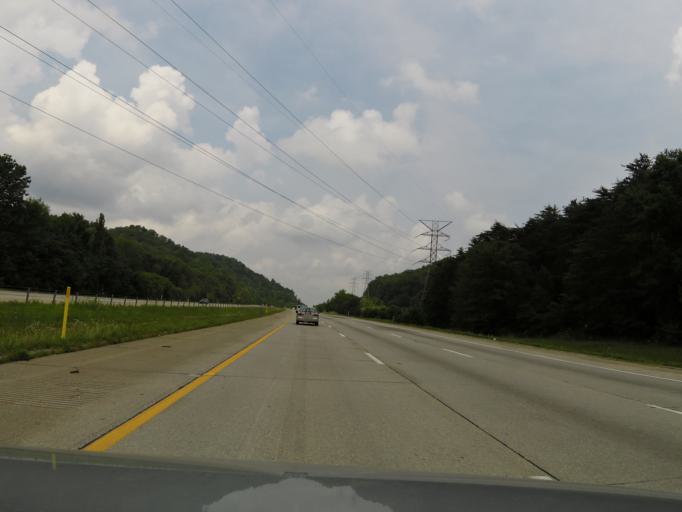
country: US
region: Kentucky
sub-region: Bullitt County
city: Lebanon Junction
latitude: 37.8742
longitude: -85.7029
